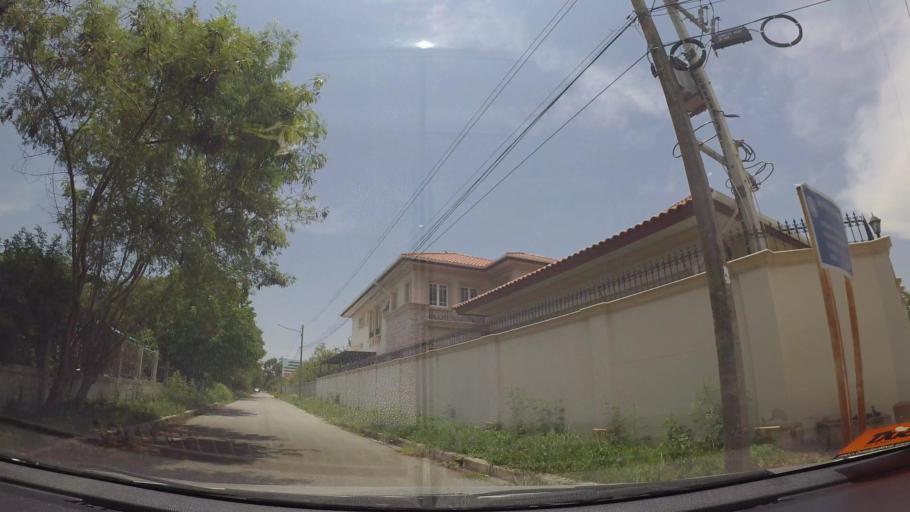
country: TH
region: Chon Buri
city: Chon Buri
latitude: 13.3396
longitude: 100.9539
